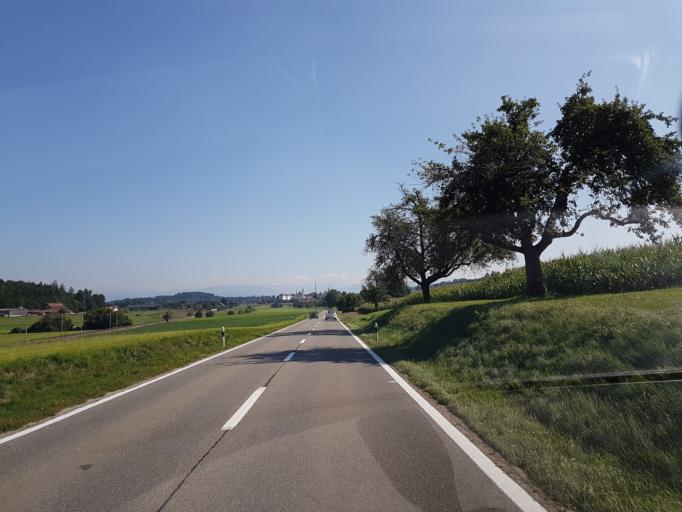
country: CH
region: Aargau
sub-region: Bezirk Muri
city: Muri
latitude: 47.2922
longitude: 8.3218
